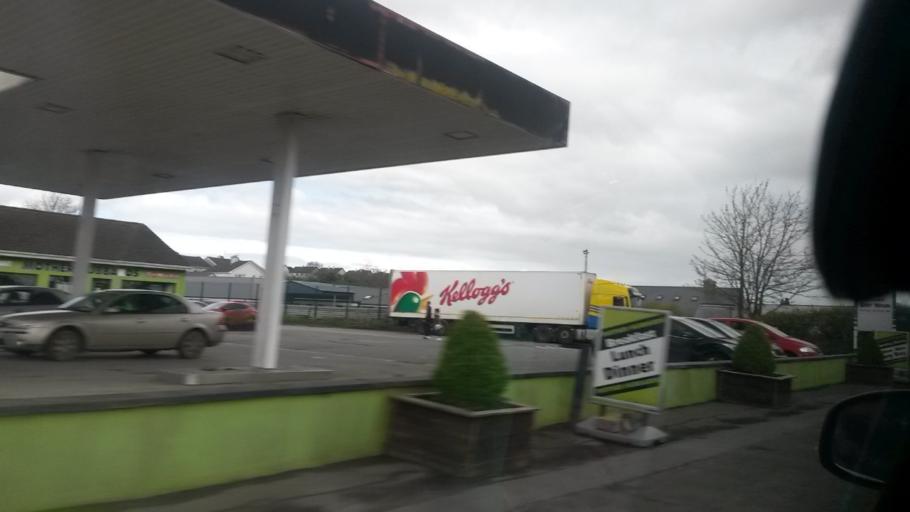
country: IE
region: Munster
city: Cashel
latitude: 52.5069
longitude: -7.8911
